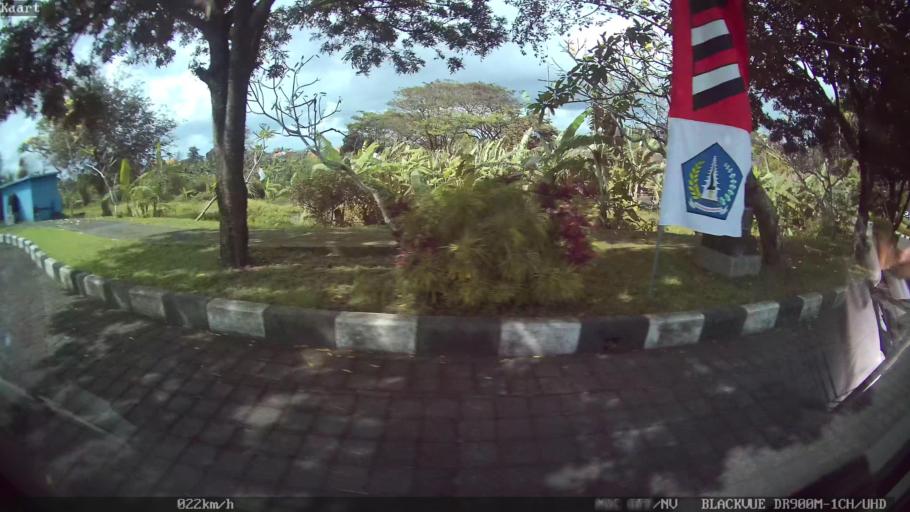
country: ID
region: Bali
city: Banjar Karangsuling
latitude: -8.6013
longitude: 115.1813
